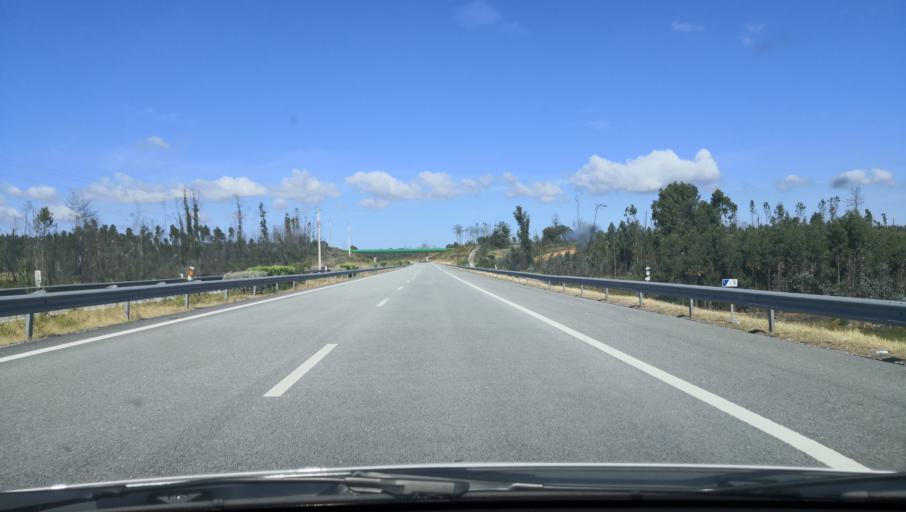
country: PT
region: Coimbra
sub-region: Cantanhede
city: Cantanhede
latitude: 40.2854
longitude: -8.5647
